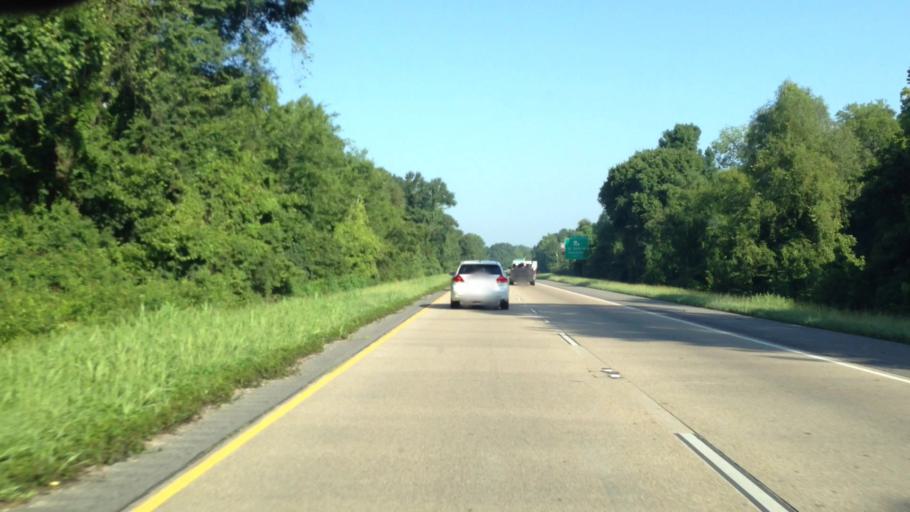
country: US
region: Louisiana
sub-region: Ascension Parish
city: Gonzales
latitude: 30.1972
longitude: -90.9294
